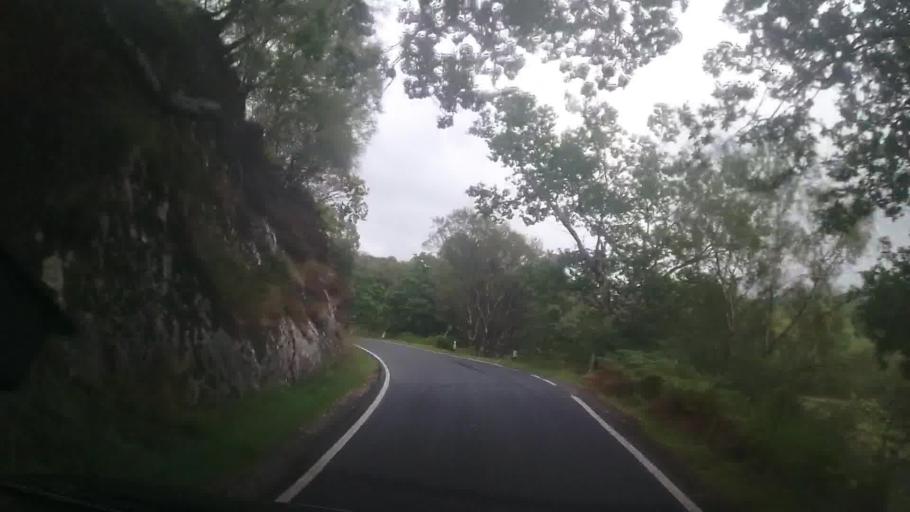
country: GB
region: Scotland
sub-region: Argyll and Bute
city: Isle Of Mull
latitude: 56.6782
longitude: -5.8419
